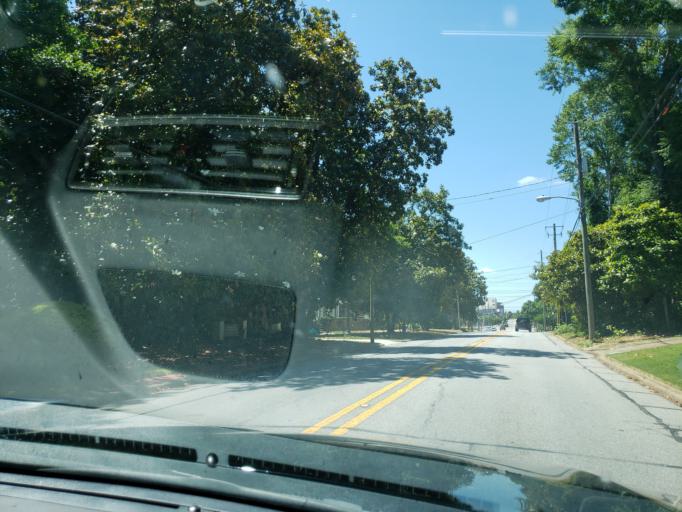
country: US
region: Alabama
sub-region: Lee County
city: Auburn
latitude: 32.6123
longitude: -85.4817
